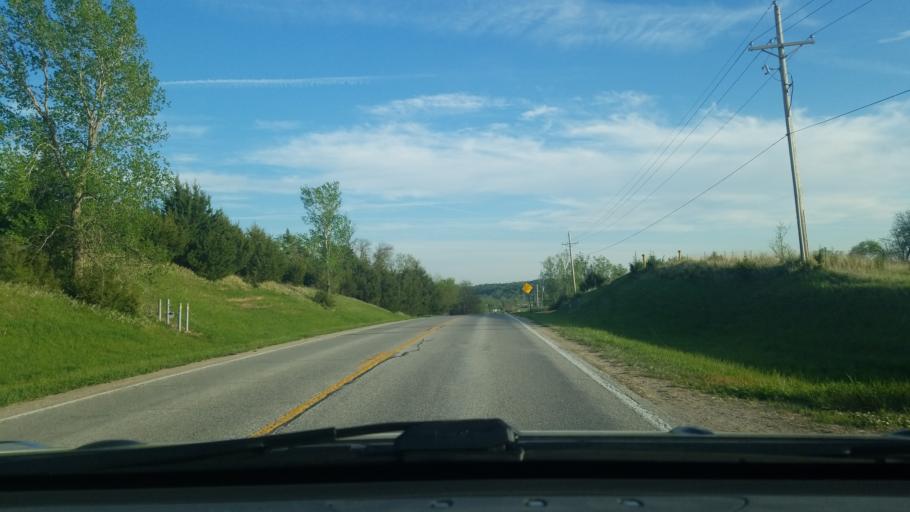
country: US
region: Nebraska
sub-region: Sarpy County
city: Offutt Air Force Base
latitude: 41.0760
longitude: -95.9663
